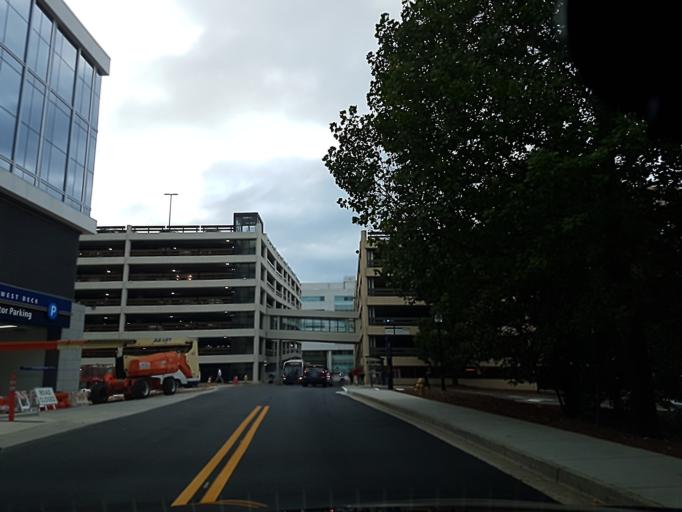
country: US
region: Georgia
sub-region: DeKalb County
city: North Decatur
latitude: 33.7906
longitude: -84.3201
